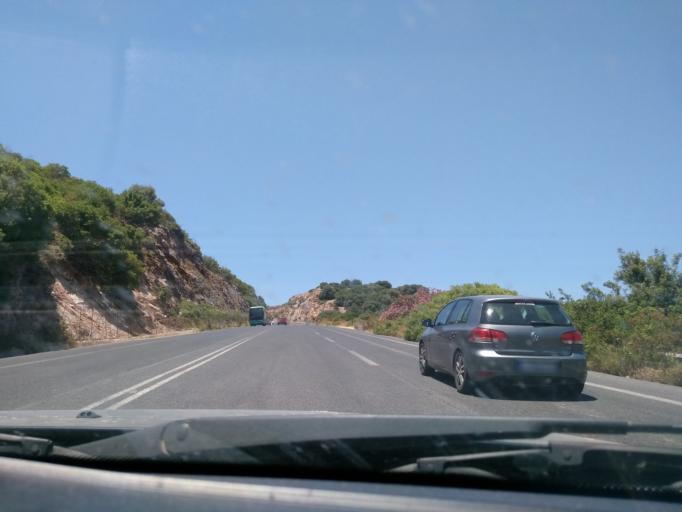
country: GR
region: Crete
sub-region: Nomos Rethymnis
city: Anogeia
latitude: 35.3875
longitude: 24.9153
